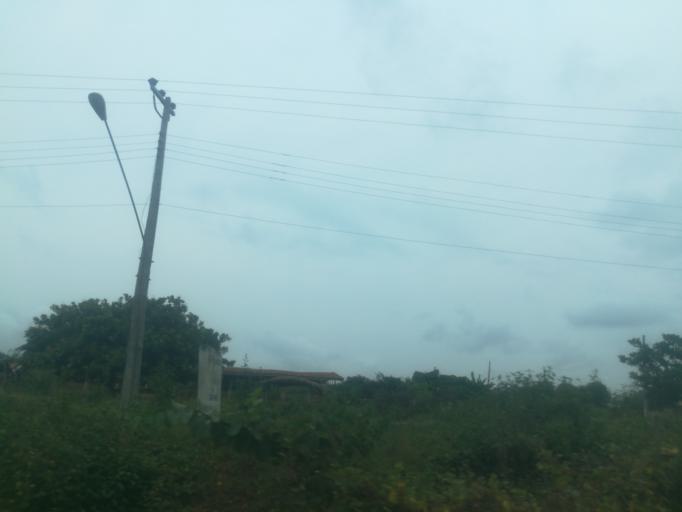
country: NG
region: Ogun
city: Ayetoro
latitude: 7.1069
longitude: 3.1389
